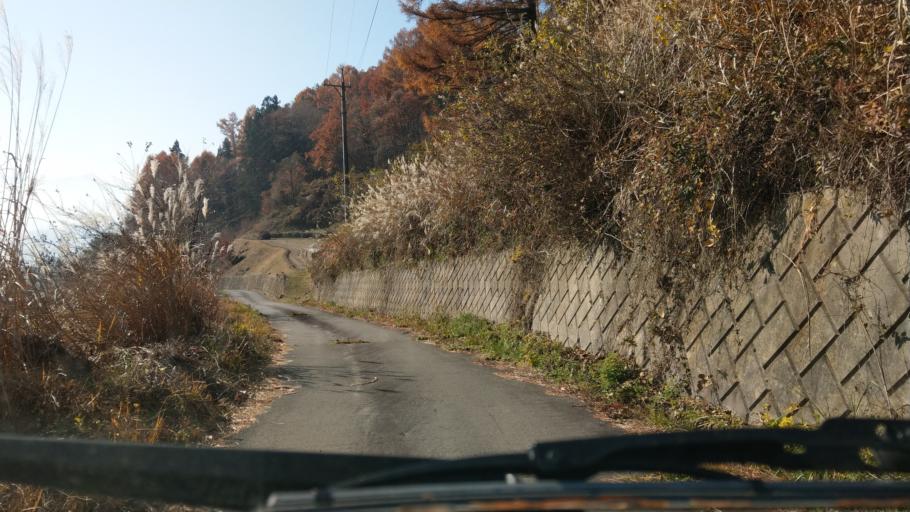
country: JP
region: Nagano
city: Komoro
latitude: 36.3604
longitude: 138.4390
